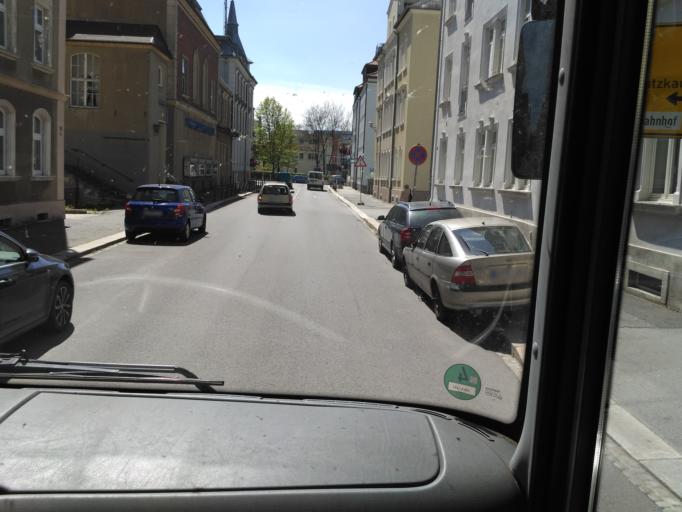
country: DE
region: Saxony
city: Bischofswerda
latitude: 51.1265
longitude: 14.1838
